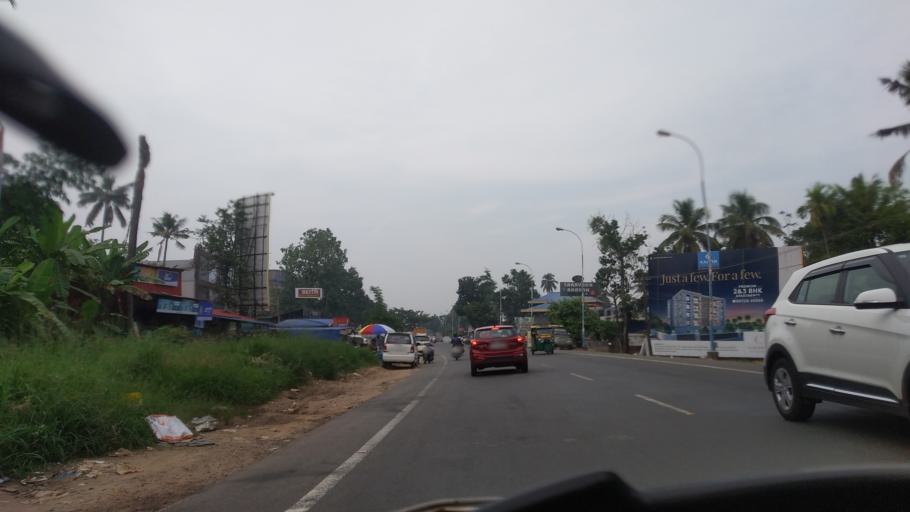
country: IN
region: Kerala
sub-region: Ernakulam
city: Elur
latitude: 10.0448
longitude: 76.2981
